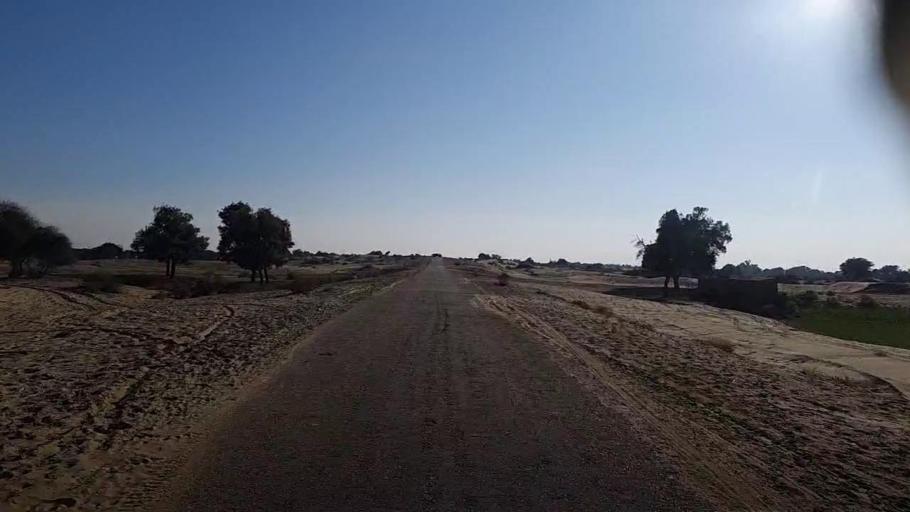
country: PK
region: Sindh
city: Khairpur
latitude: 27.9043
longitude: 69.7495
